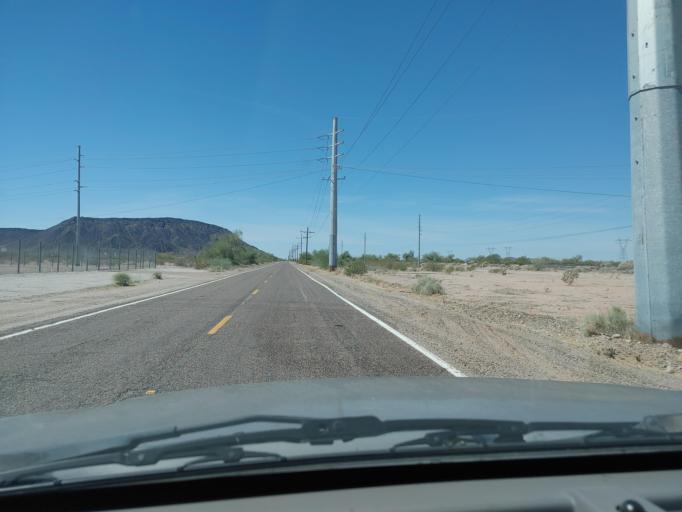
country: US
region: Arizona
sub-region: Maricopa County
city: Gila Bend
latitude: 33.0262
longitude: -113.3281
